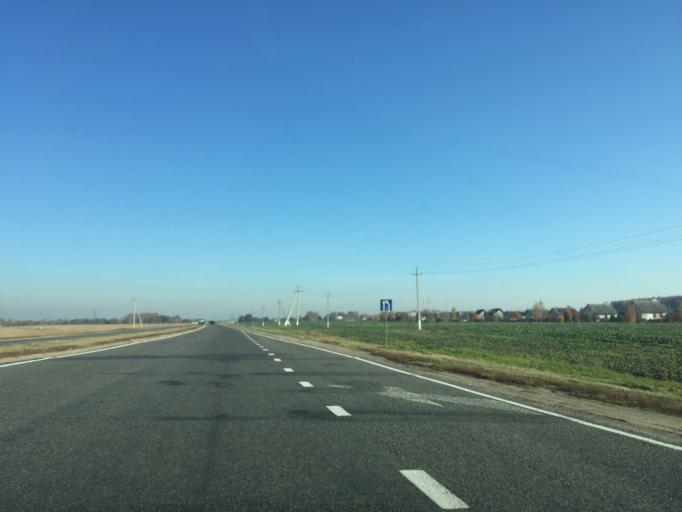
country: BY
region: Mogilev
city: Buynichy
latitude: 53.9517
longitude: 30.2281
